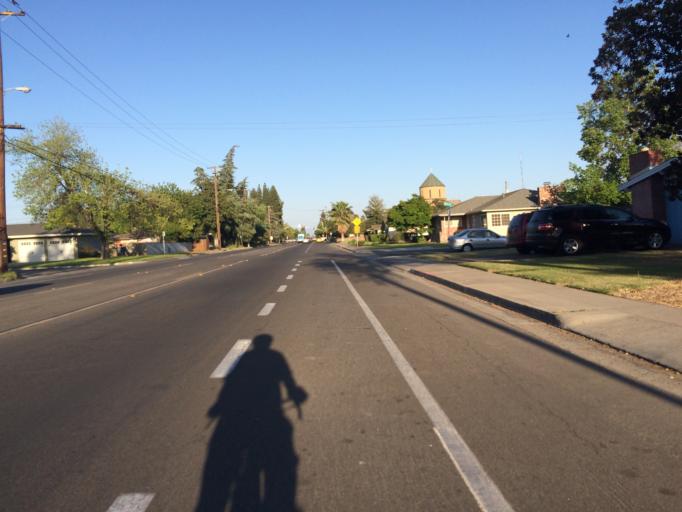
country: US
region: California
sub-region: Fresno County
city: Fresno
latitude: 36.7868
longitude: -119.7755
